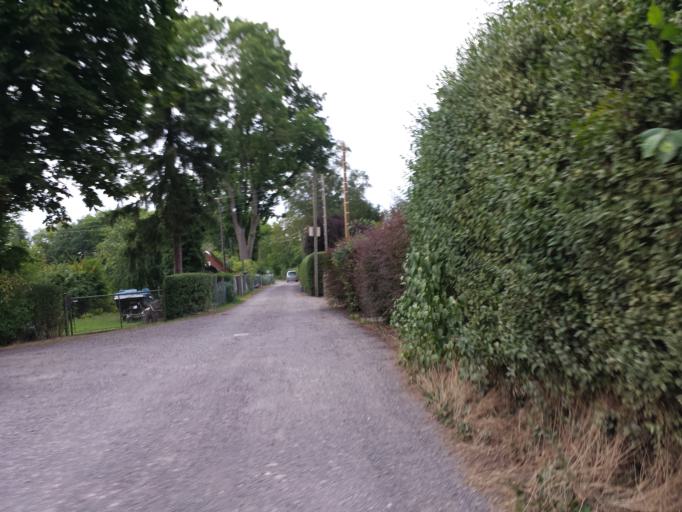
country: DE
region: Lower Saxony
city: Stuhr
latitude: 53.0678
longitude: 8.7623
